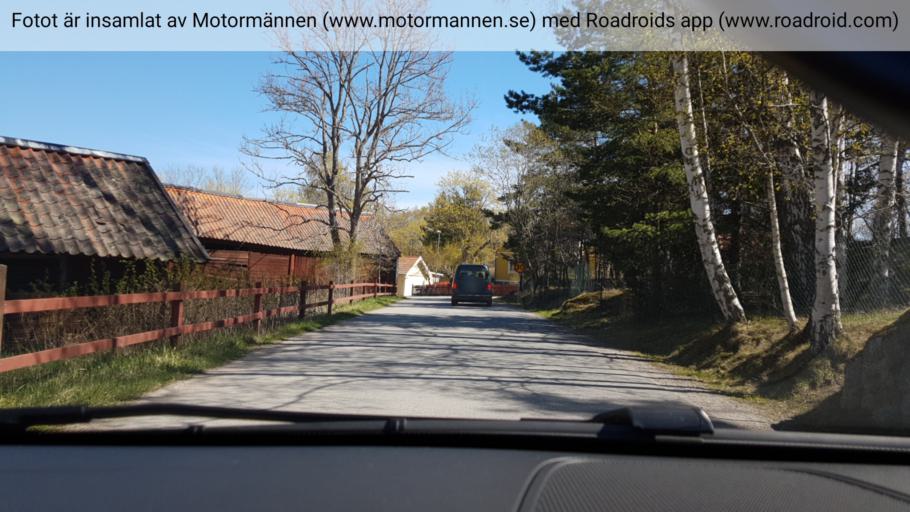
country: SE
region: Stockholm
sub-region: Varmdo Kommun
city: Holo
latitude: 59.2900
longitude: 18.6883
